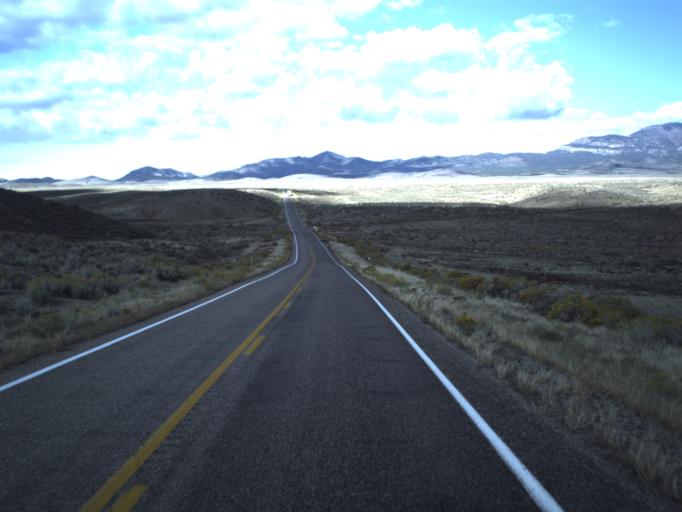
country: US
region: Utah
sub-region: Beaver County
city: Milford
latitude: 38.4383
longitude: -113.1494
